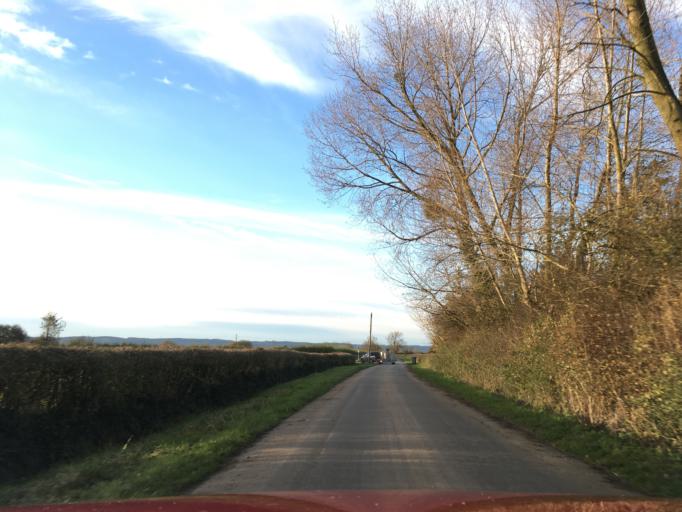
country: GB
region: England
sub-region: South Gloucestershire
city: Hill
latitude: 51.6543
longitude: -2.5246
